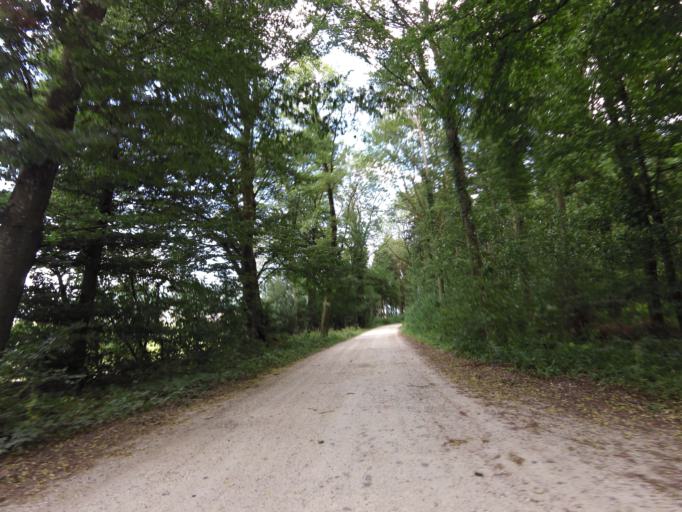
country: CH
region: Solothurn
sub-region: Bezirk Gaeu
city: Oensingen
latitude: 47.2683
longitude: 7.7247
